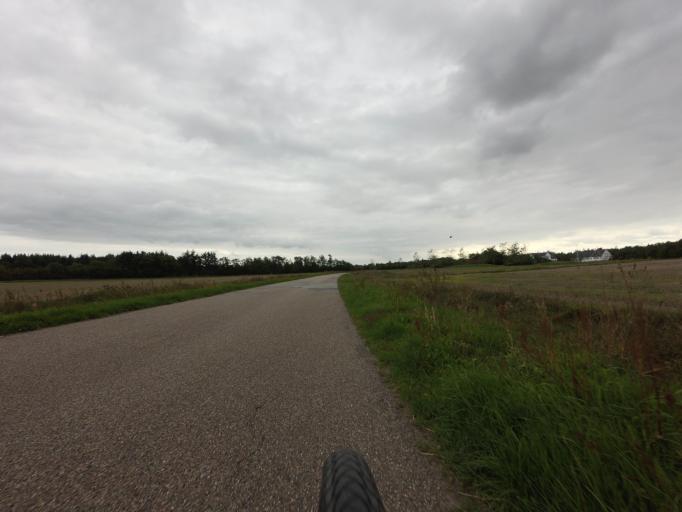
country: DK
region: North Denmark
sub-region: Hjorring Kommune
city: Hirtshals
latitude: 57.5688
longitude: 10.0329
